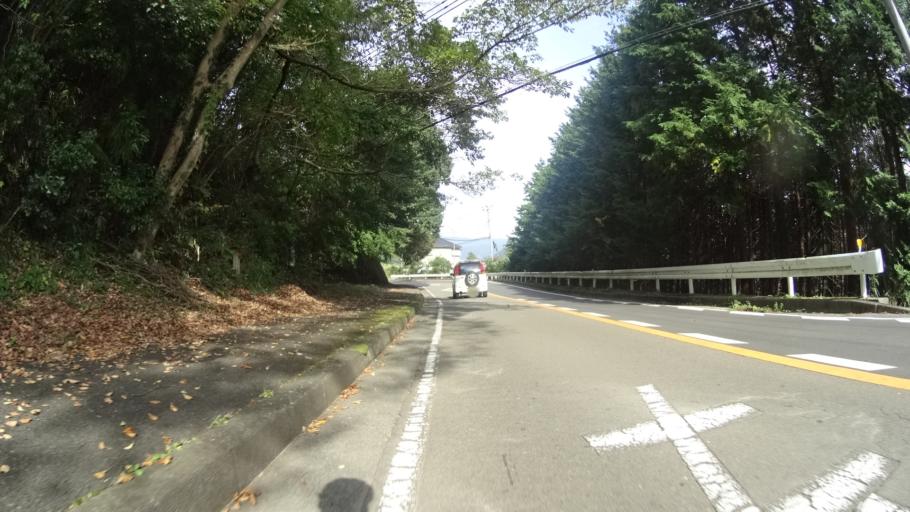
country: JP
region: Yamanashi
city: Uenohara
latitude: 35.5839
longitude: 139.1453
